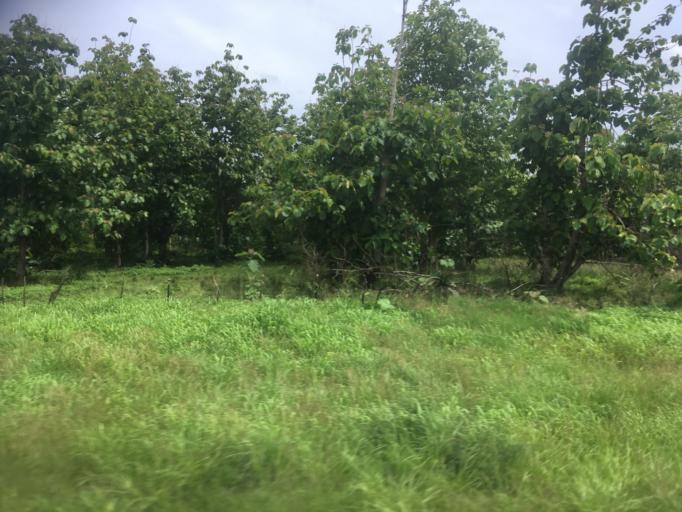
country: CU
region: Matanzas
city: Jovellanos
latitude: 22.7904
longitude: -81.1153
